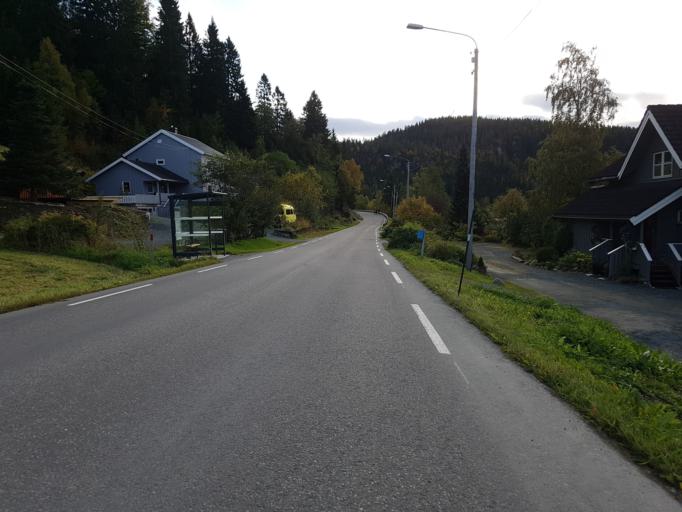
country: NO
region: Sor-Trondelag
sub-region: Klaebu
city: Klaebu
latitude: 63.3972
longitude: 10.5241
